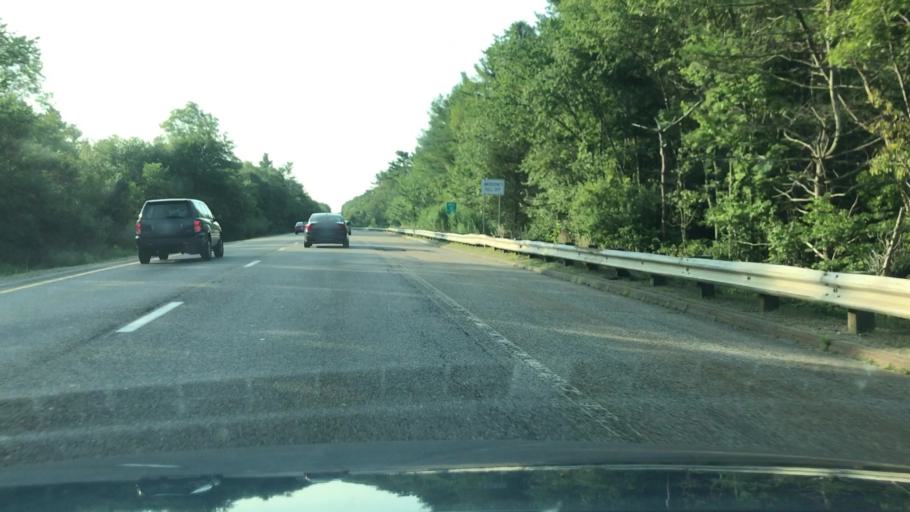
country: US
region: Massachusetts
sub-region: Plymouth County
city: Hanover
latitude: 42.1392
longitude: -70.8232
